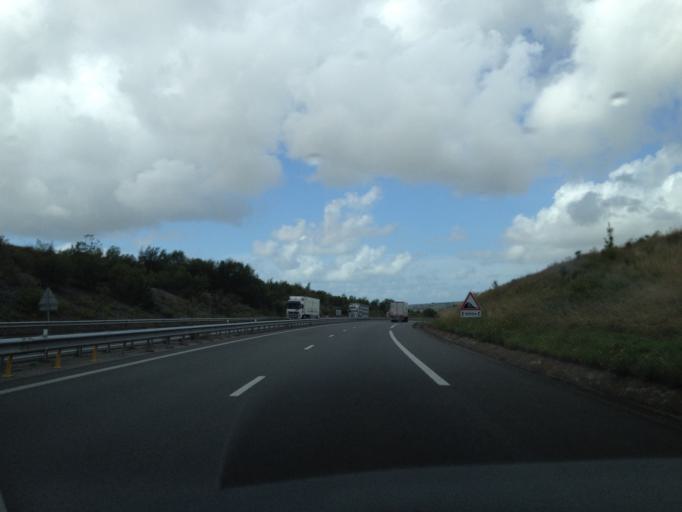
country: FR
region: Nord-Pas-de-Calais
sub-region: Departement du Pas-de-Calais
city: Isques
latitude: 50.6572
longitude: 1.6562
